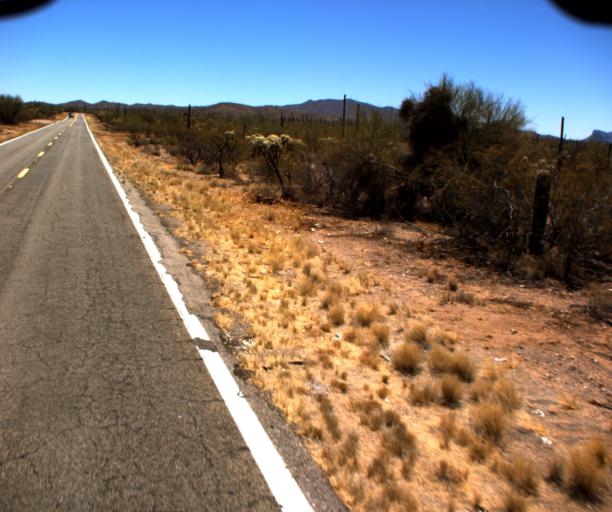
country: US
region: Arizona
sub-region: Pima County
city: Sells
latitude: 32.1768
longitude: -112.2424
